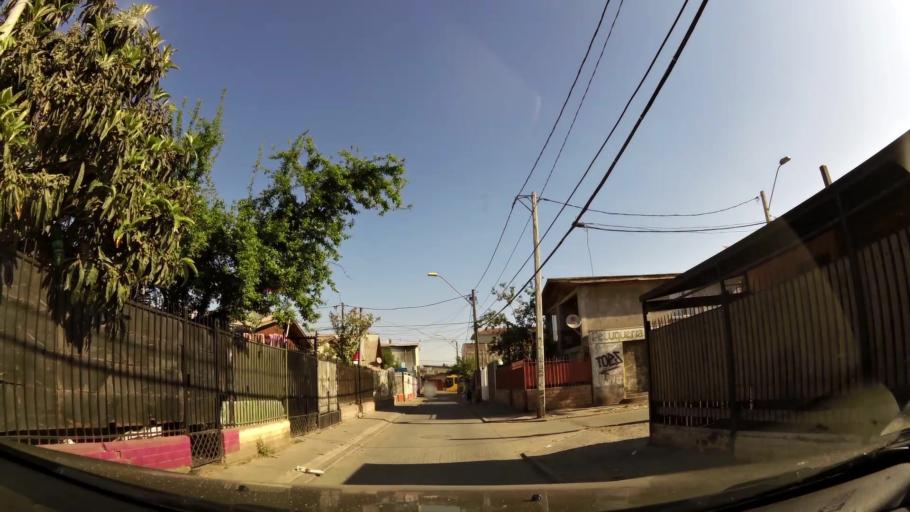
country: CL
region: Santiago Metropolitan
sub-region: Provincia de Santiago
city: La Pintana
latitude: -33.5775
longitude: -70.6539
